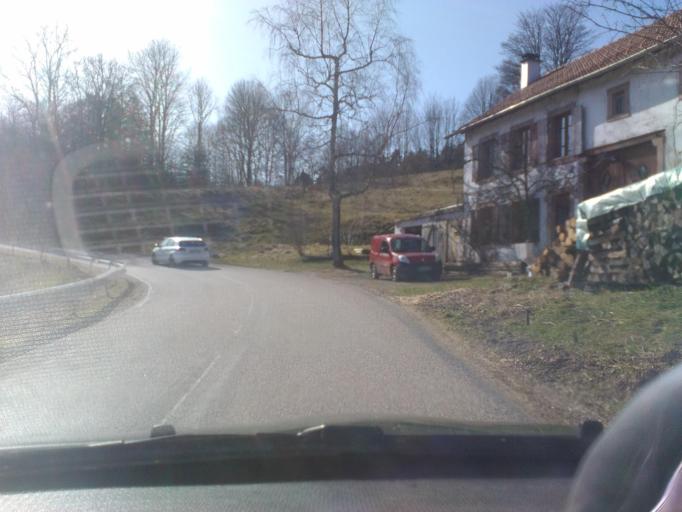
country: FR
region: Lorraine
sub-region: Departement des Vosges
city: Ban-de-Laveline
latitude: 48.3389
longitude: 7.0555
